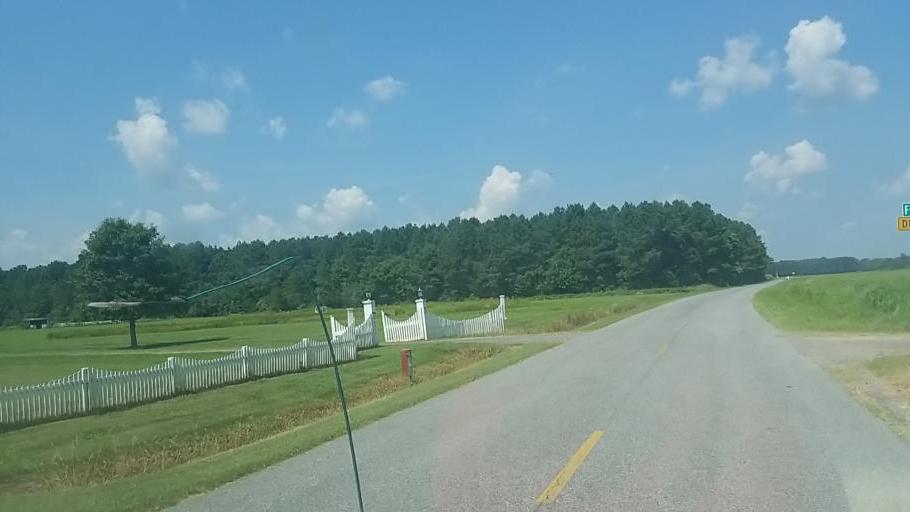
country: US
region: Maryland
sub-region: Worcester County
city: Berlin
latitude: 38.2968
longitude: -75.2657
